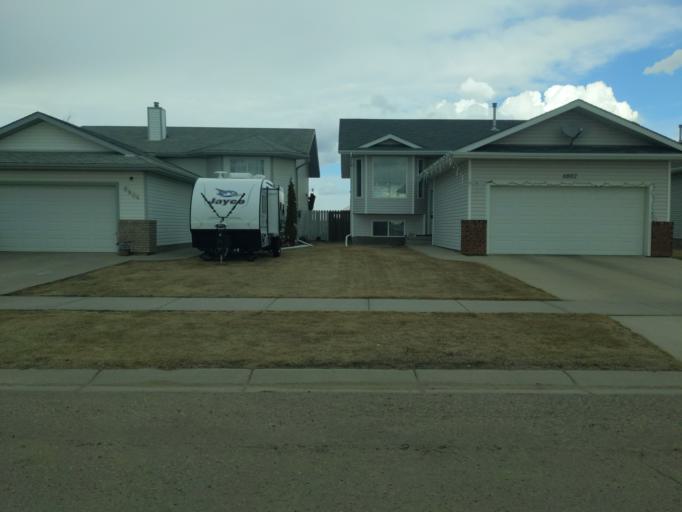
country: CA
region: Saskatchewan
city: Lloydminster
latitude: 53.2690
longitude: -110.0437
